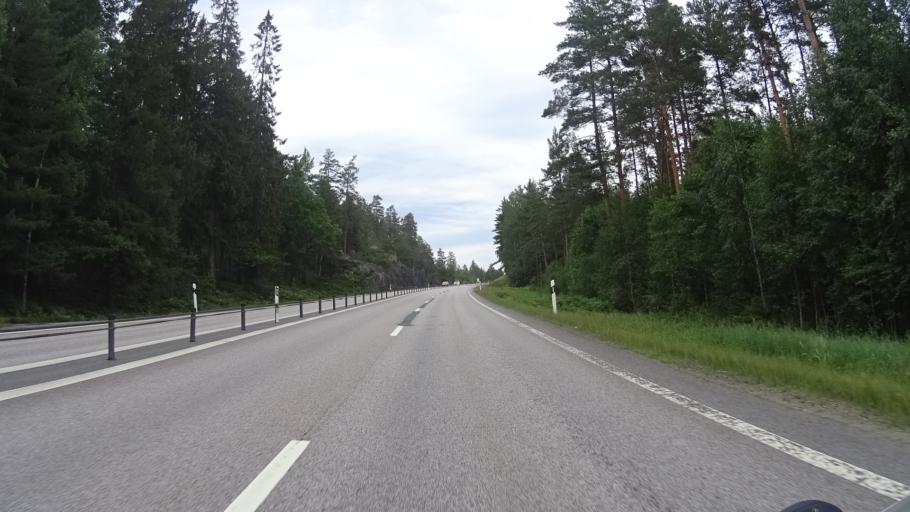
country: SE
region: Kalmar
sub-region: Vasterviks Kommun
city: Forserum
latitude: 58.0356
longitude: 16.5164
